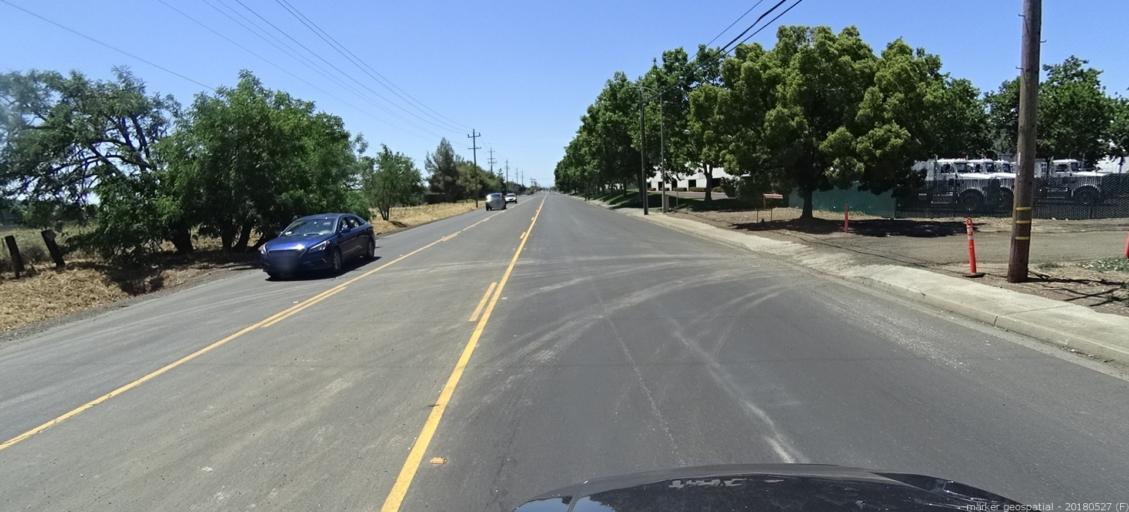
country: US
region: California
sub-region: Sacramento County
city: Florin
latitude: 38.5107
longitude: -121.3800
